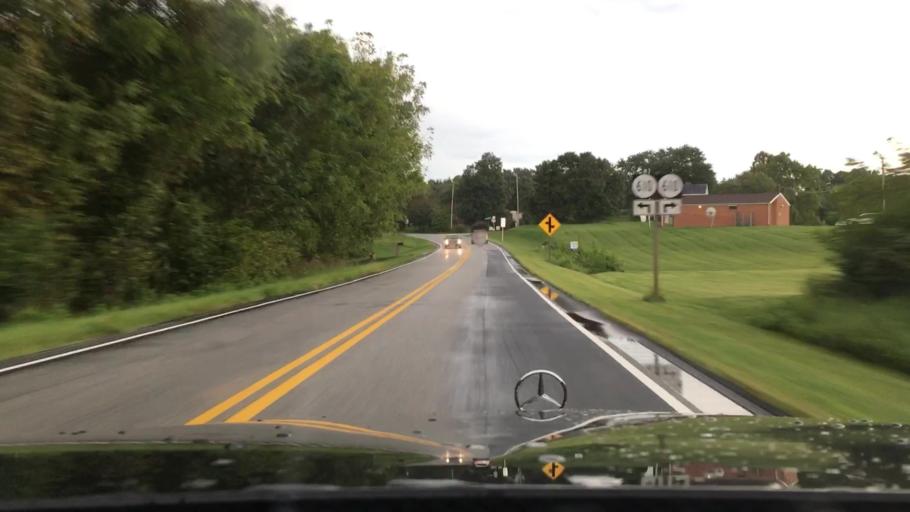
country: US
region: Virginia
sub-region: Amherst County
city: Amherst
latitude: 37.6455
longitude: -79.0213
